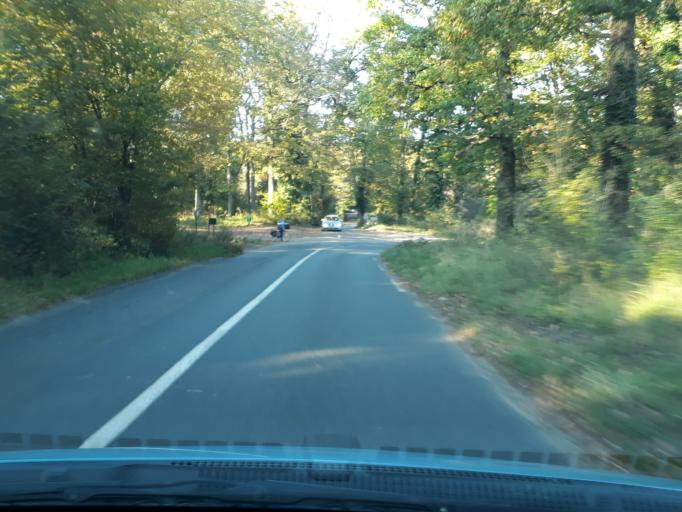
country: FR
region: Ile-de-France
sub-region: Departement de Seine-et-Marne
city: Fontainebleau
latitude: 48.4177
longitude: 2.6982
